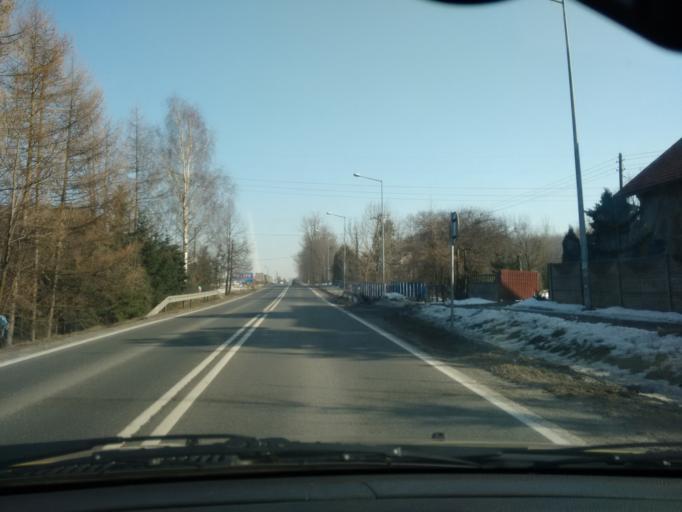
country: PL
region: Silesian Voivodeship
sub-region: Powiat bielski
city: Czaniec
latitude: 49.8804
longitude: 19.2551
